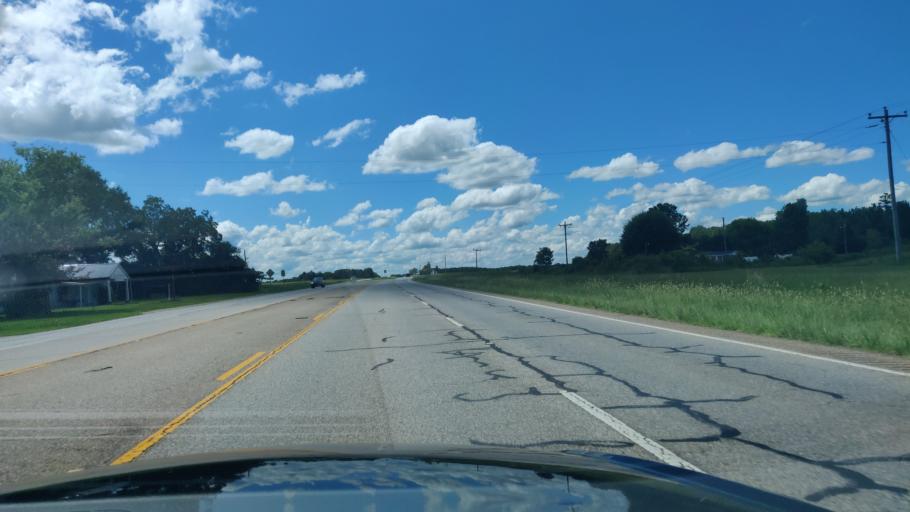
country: US
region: Georgia
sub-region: Stewart County
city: Richland
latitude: 31.9848
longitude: -84.6263
